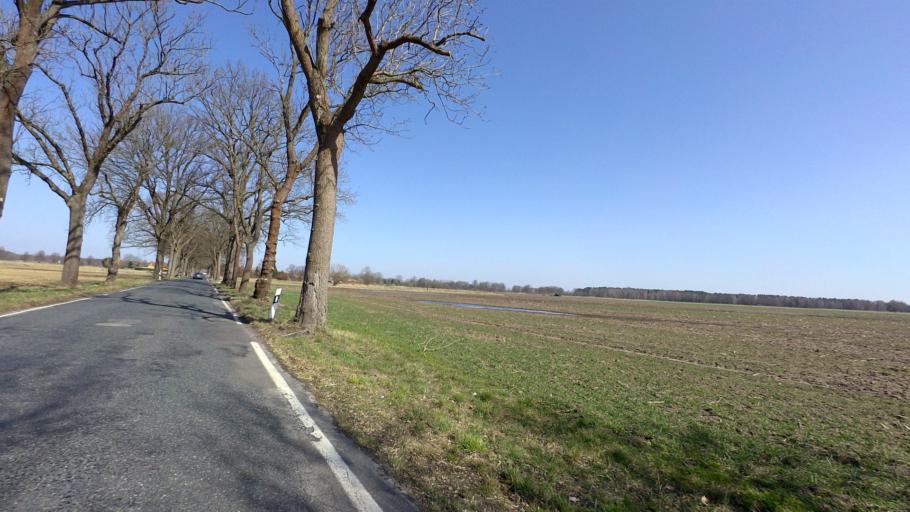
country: DE
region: Brandenburg
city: Lindow
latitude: 52.9273
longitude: 12.9652
